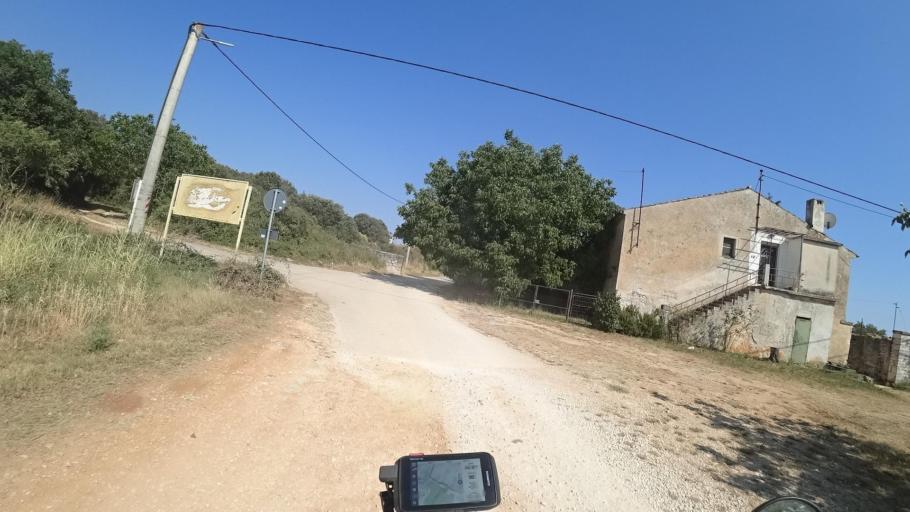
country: HR
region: Istarska
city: Fazana
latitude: 44.9925
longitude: 13.7418
